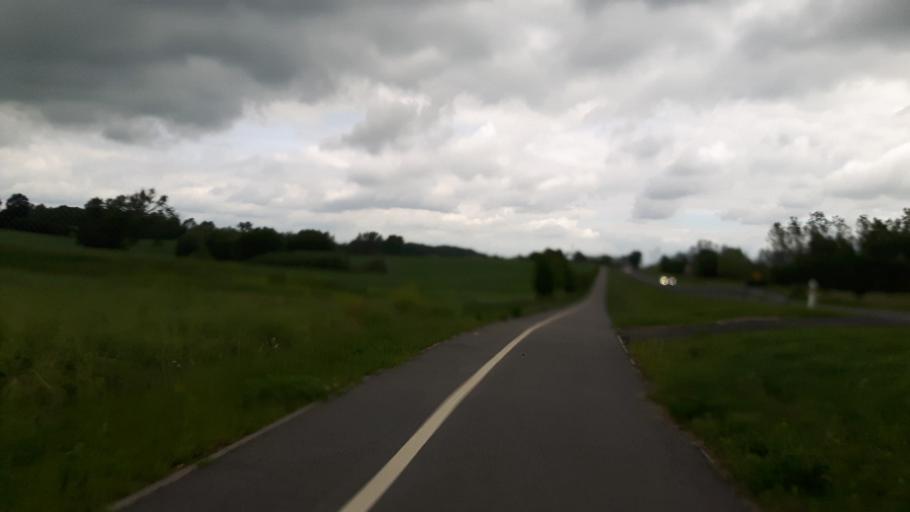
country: PL
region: West Pomeranian Voivodeship
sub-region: Powiat policki
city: Kolbaskowo
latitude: 53.3298
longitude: 14.4273
